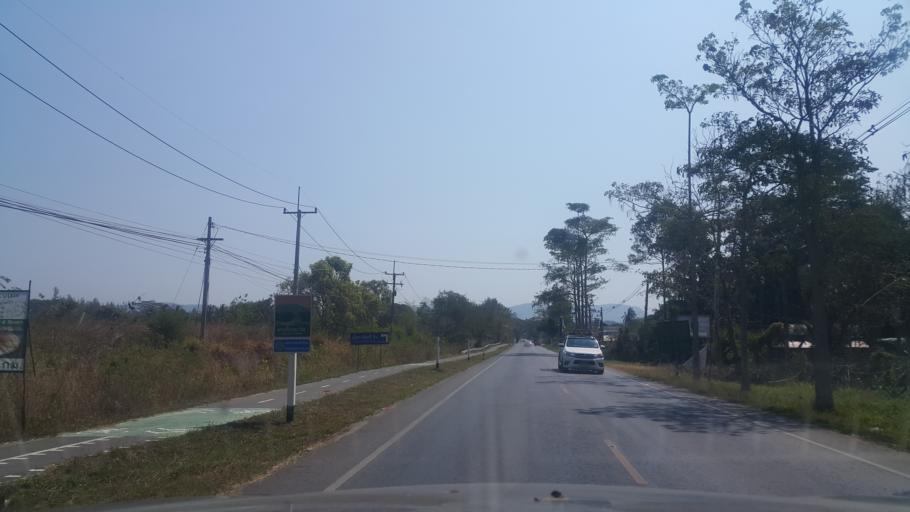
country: TH
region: Nakhon Ratchasima
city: Wang Nam Khiao
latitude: 14.3692
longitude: 101.8872
